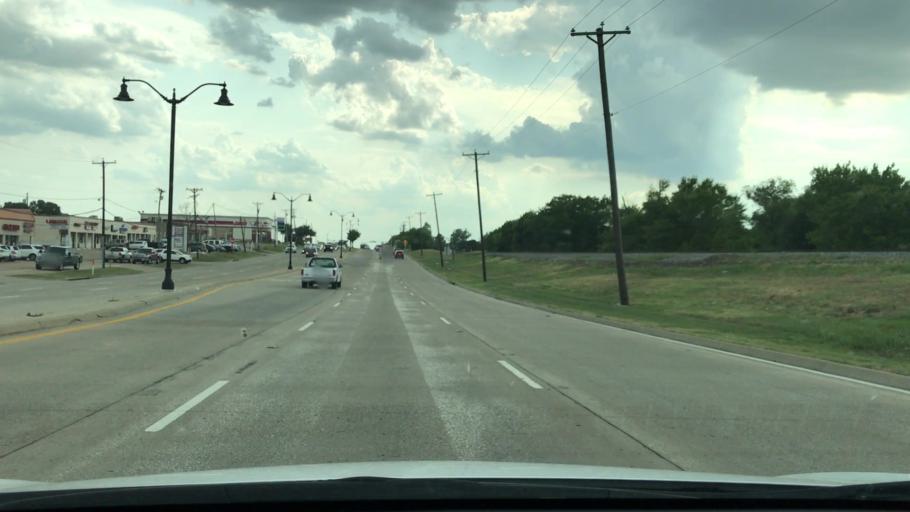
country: US
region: Texas
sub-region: Dallas County
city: Sachse
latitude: 32.9753
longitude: -96.5972
